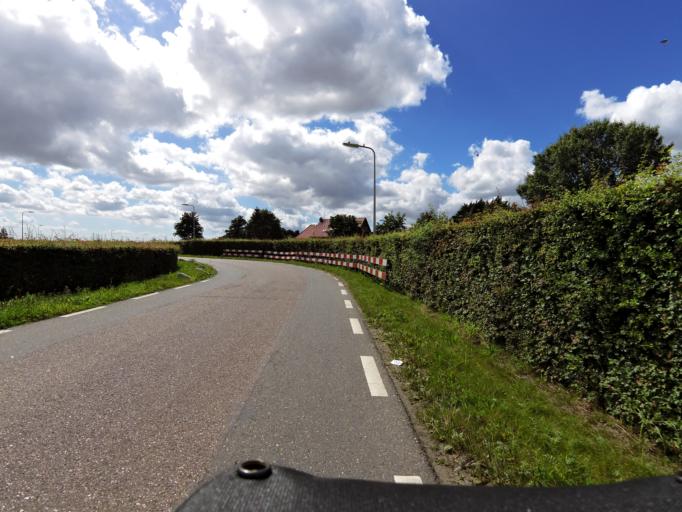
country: NL
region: South Holland
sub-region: Gemeente Oud-Beijerland
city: Oud-Beijerland
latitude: 51.8270
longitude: 4.3702
